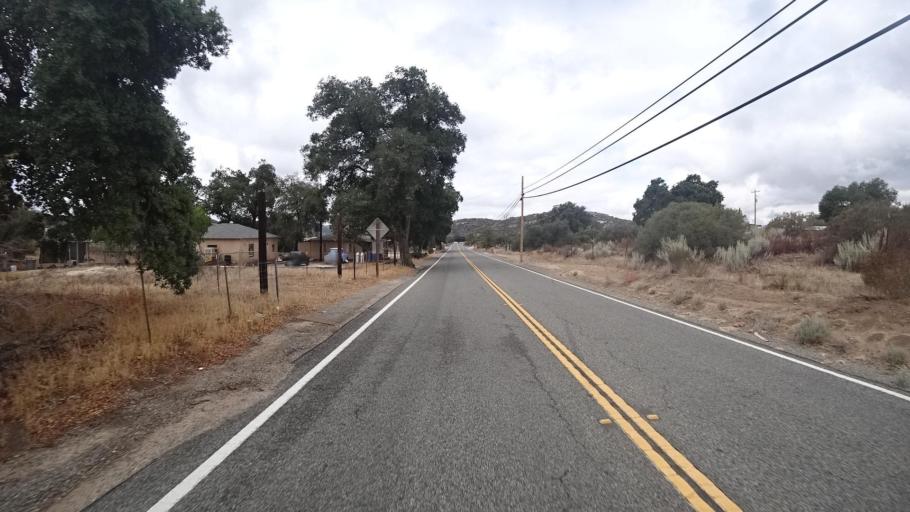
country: US
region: California
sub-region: San Diego County
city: Campo
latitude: 32.6424
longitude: -116.4269
